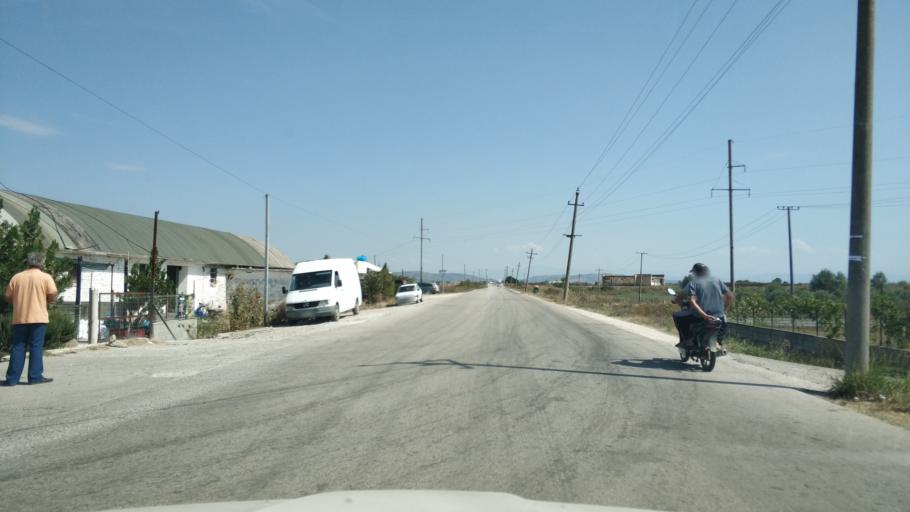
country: AL
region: Fier
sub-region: Rrethi i Lushnjes
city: Gradishte
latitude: 40.8848
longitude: 19.5902
